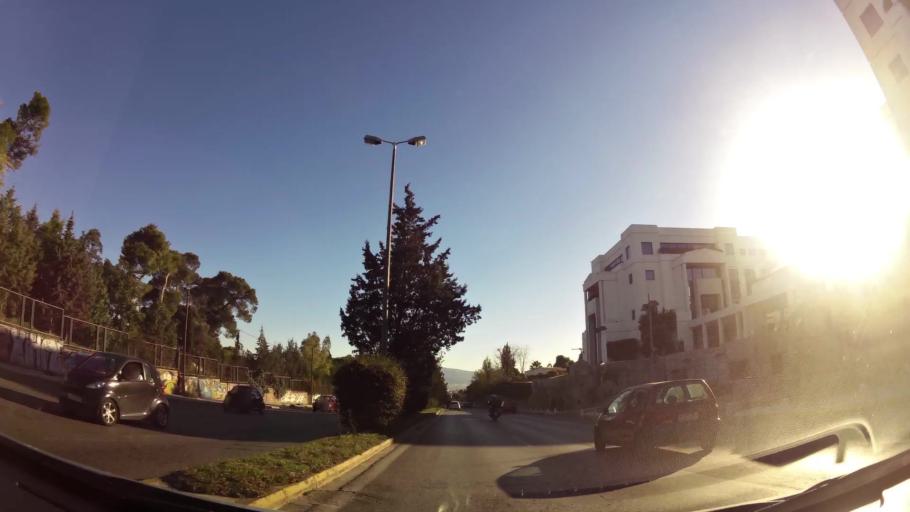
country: GR
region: Attica
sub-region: Nomarchia Athinas
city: Kifisia
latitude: 38.0631
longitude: 23.8092
